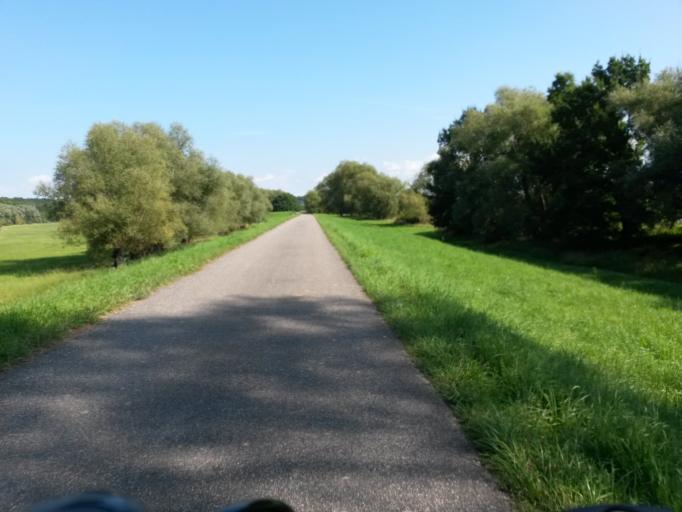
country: DE
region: Brandenburg
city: Schoneberg
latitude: 52.9660
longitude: 14.1113
